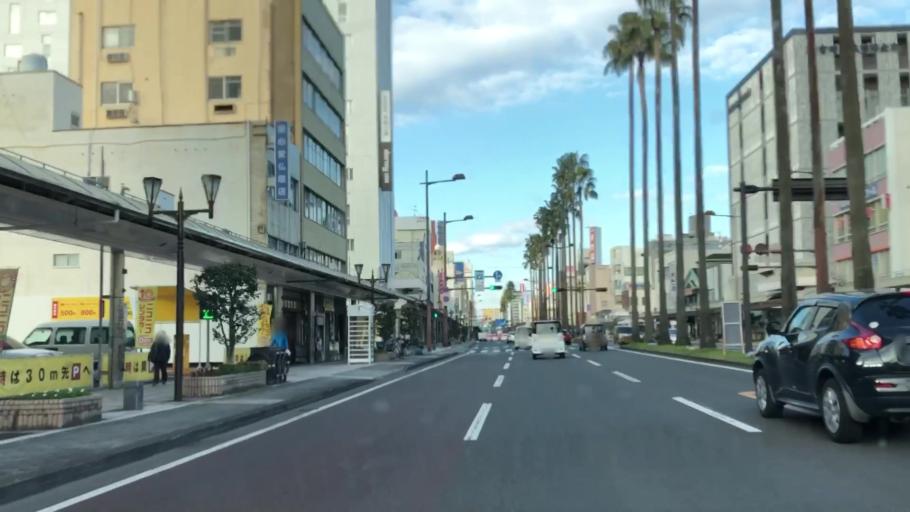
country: JP
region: Miyazaki
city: Miyazaki-shi
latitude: 31.9109
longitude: 131.4221
